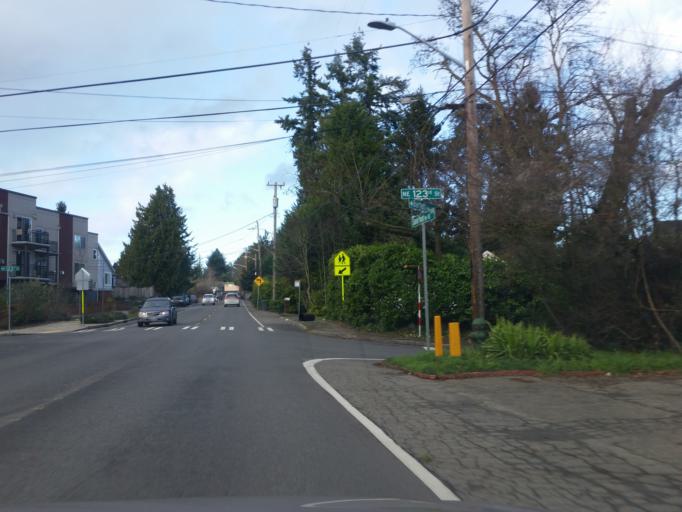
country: US
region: Washington
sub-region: King County
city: Lake Forest Park
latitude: 47.7171
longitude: -122.2837
